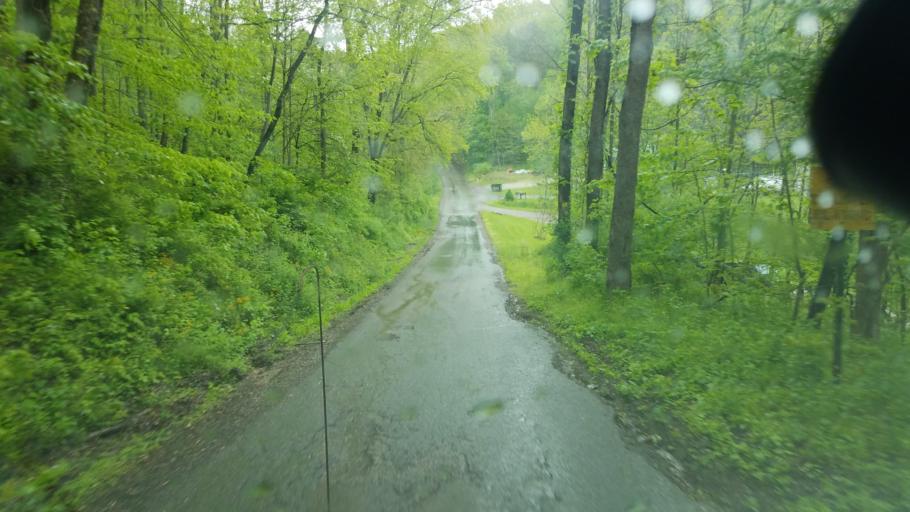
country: US
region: Ohio
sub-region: Muskingum County
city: Frazeysburg
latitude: 40.1481
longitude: -82.0983
